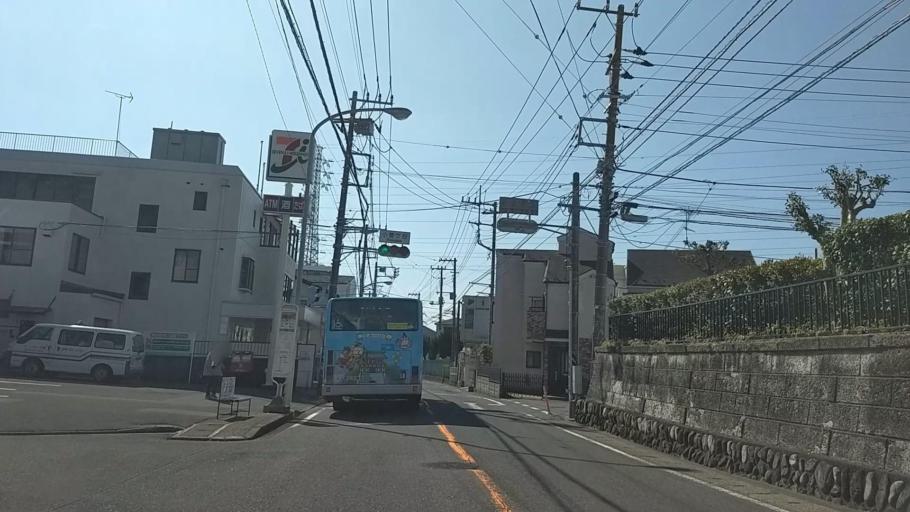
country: JP
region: Kanagawa
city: Kamakura
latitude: 35.3646
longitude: 139.5405
